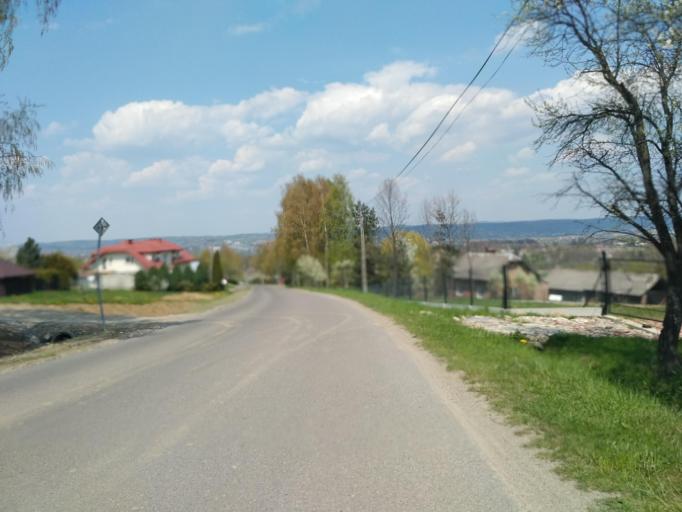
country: PL
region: Subcarpathian Voivodeship
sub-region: Powiat jasielski
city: Jaslo
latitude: 49.7126
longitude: 21.5067
